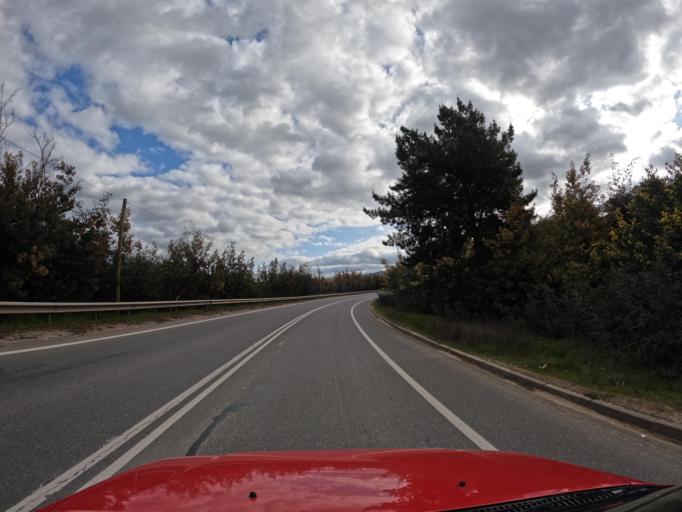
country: CL
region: Maule
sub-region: Provincia de Linares
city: San Javier
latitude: -35.5597
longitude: -72.0917
